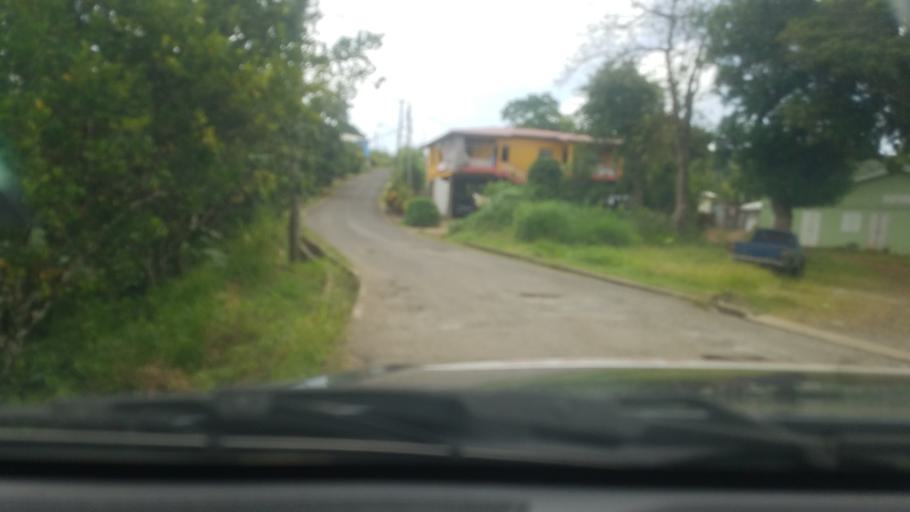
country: LC
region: Laborie Quarter
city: Laborie
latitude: 13.7911
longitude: -60.9544
